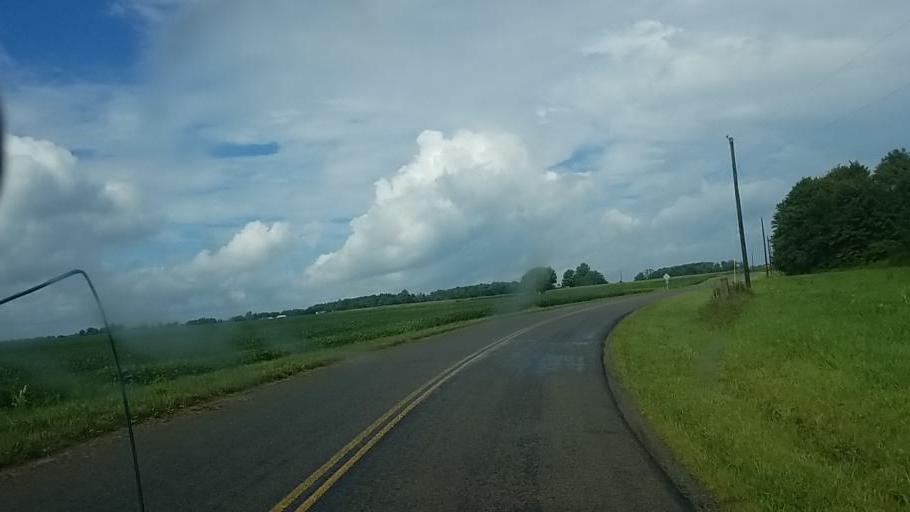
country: US
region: Ohio
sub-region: Hardin County
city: Kenton
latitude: 40.4682
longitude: -83.5120
